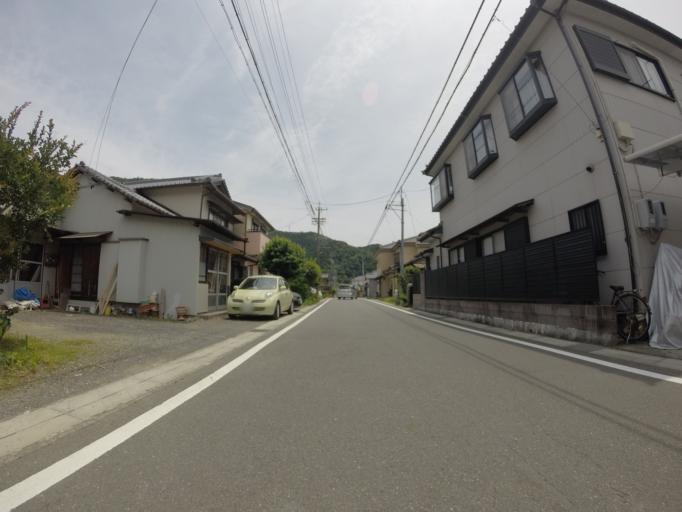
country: JP
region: Shizuoka
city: Shizuoka-shi
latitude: 35.0064
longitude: 138.2810
